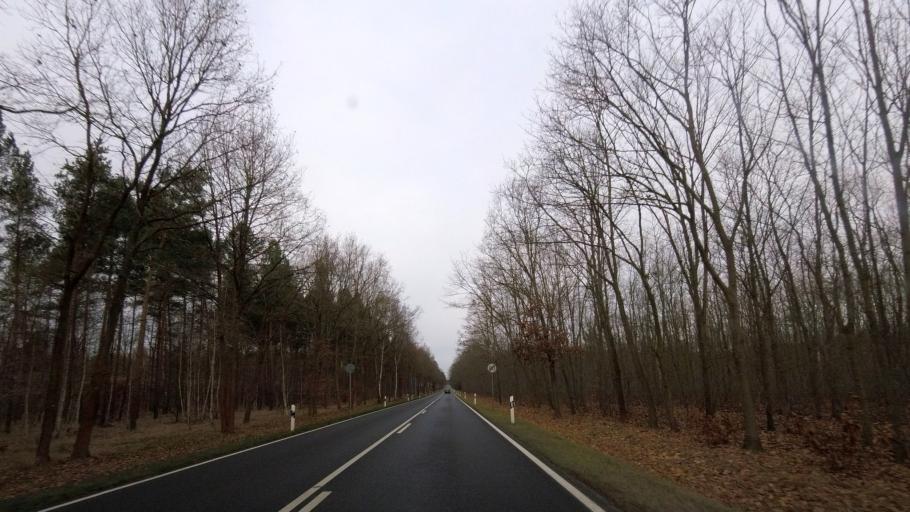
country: DE
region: Brandenburg
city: Treuenbrietzen
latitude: 52.0576
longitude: 12.9035
